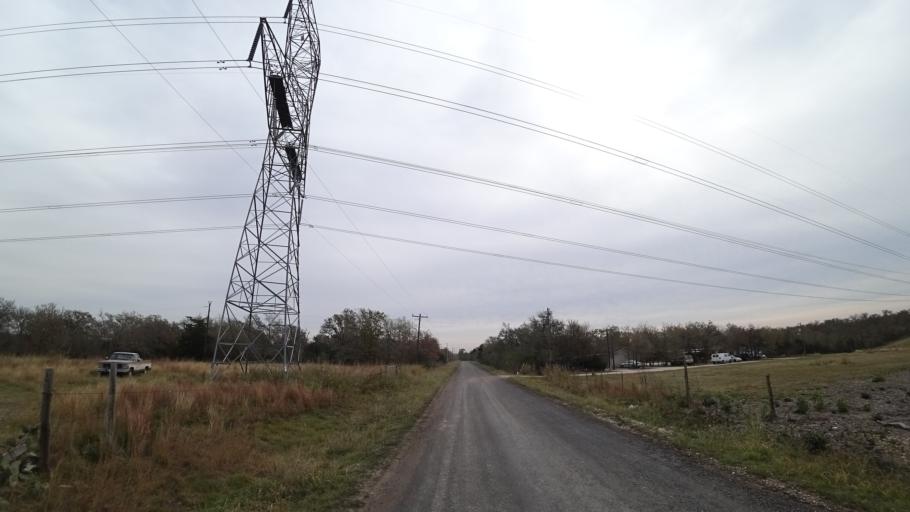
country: US
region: Texas
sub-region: Travis County
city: Garfield
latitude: 30.1047
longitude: -97.5675
